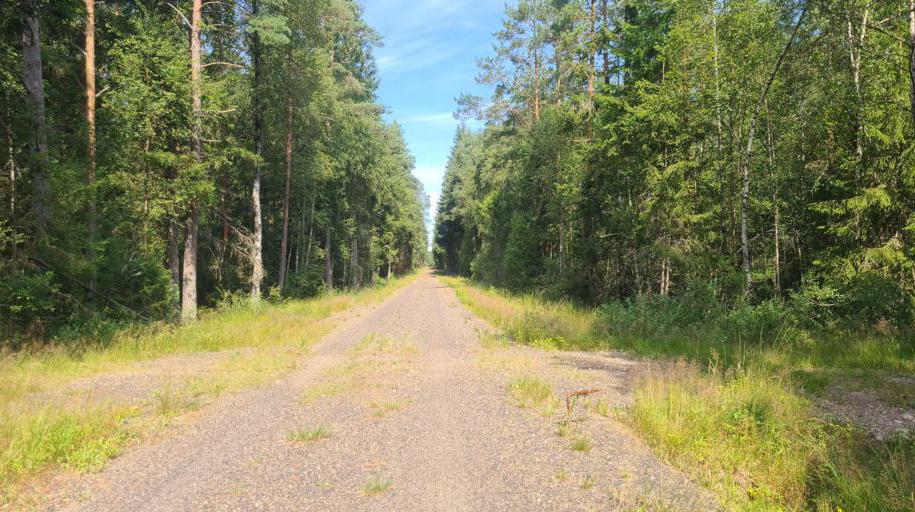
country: SE
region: Kronoberg
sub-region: Ljungby Kommun
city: Lagan
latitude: 56.9495
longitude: 13.9632
